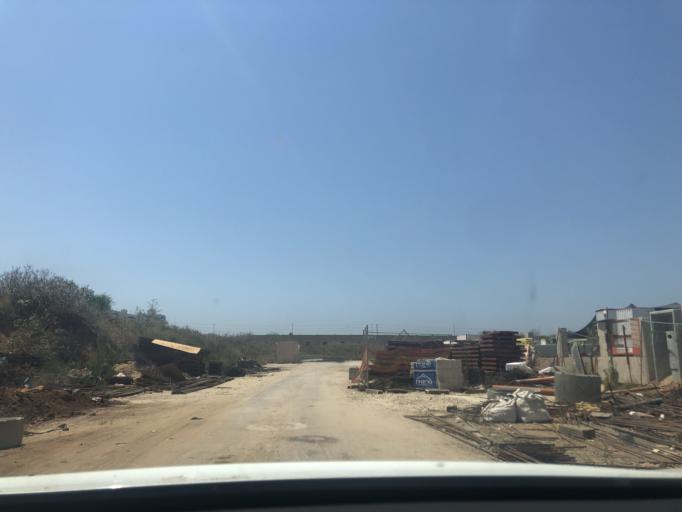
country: IL
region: Central District
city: Lod
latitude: 31.9348
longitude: 34.8952
